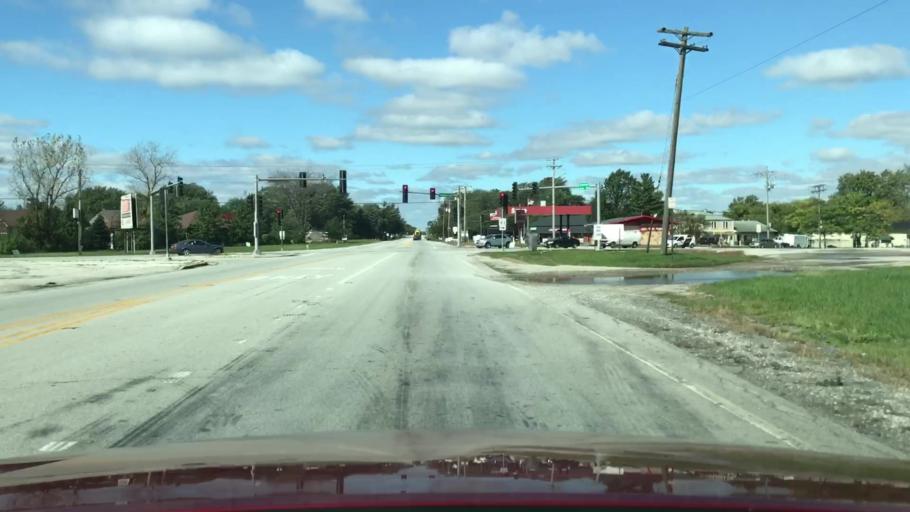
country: US
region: Illinois
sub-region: Cook County
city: Lynwood
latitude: 41.5233
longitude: -87.5575
